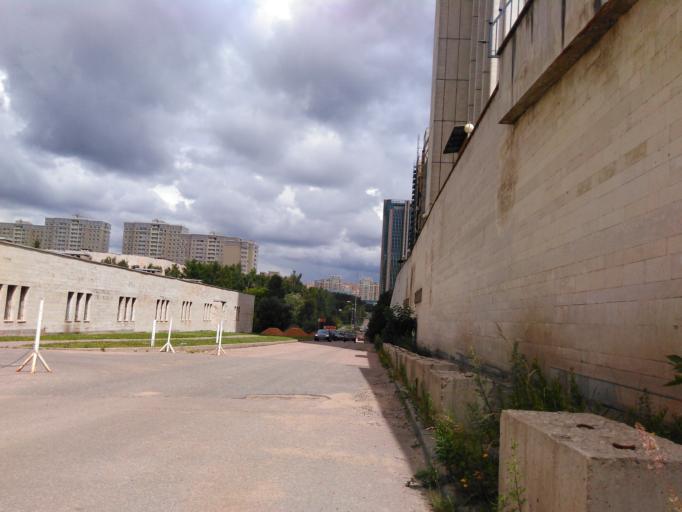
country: RU
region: Moscow
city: Ramenki
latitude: 55.6843
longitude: 37.5166
